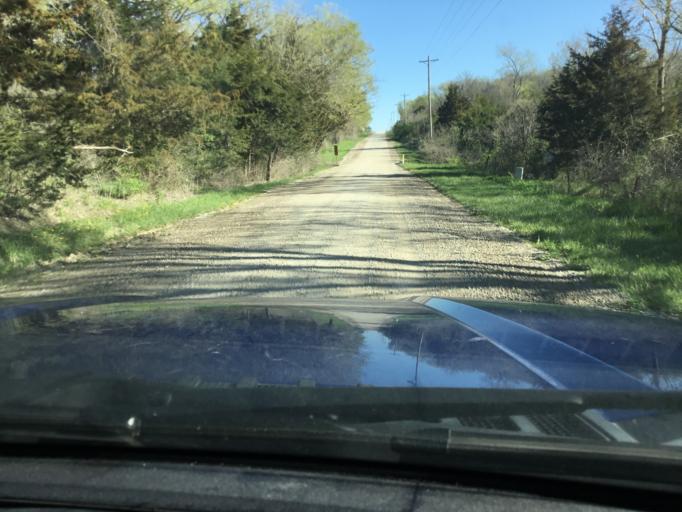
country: US
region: Kansas
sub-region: Douglas County
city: Lawrence
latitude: 38.9606
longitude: -95.3538
